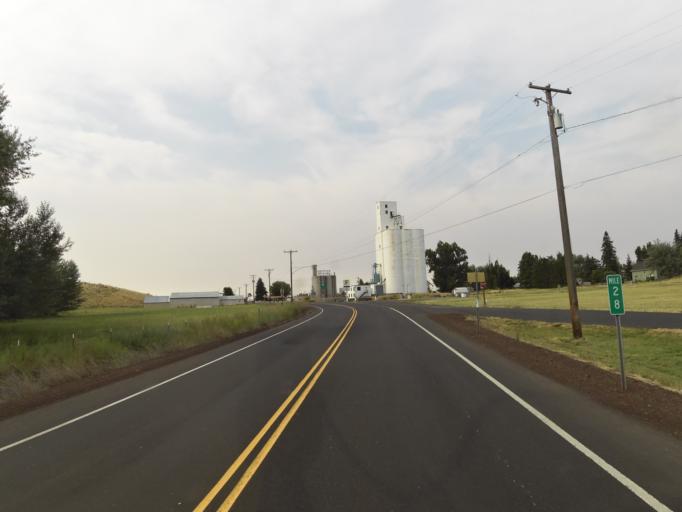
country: US
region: Oregon
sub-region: Sherman County
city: Moro
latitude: 45.3583
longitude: -120.7855
